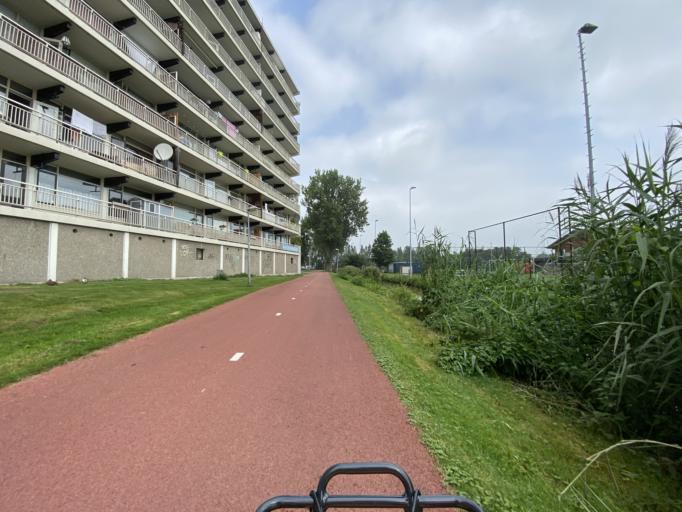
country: NL
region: North Holland
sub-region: Gemeente Weesp
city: Weesp
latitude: 52.3157
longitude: 5.0292
